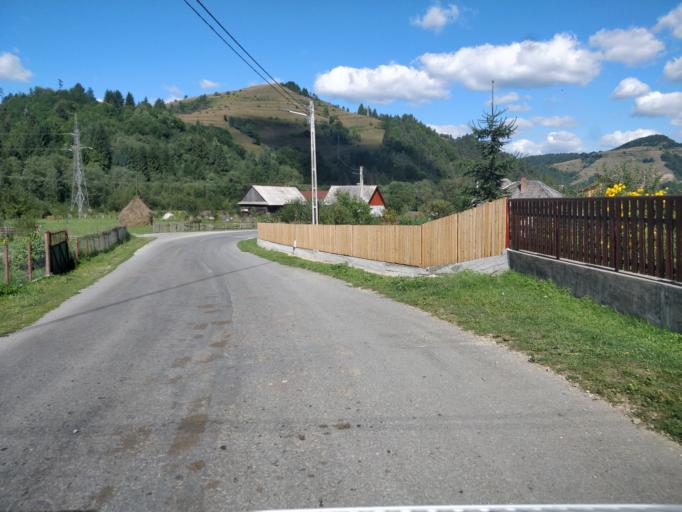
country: RO
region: Cluj
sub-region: Comuna Sacueu
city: Sacuieu
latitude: 46.8141
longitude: 22.8921
